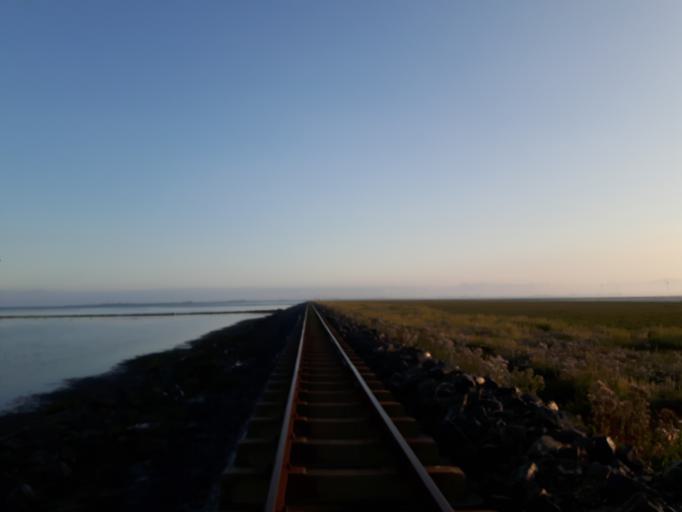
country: DE
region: Schleswig-Holstein
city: Dagebull
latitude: 54.6948
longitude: 8.7105
